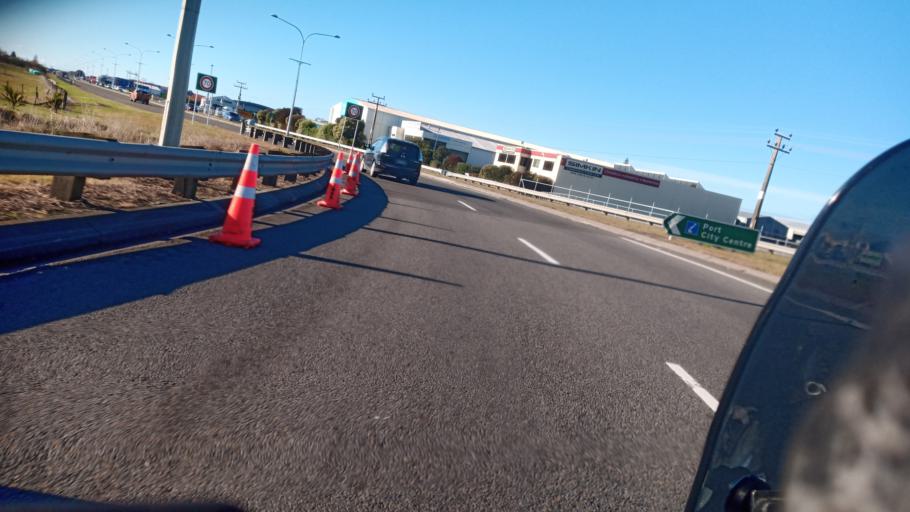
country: NZ
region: Hawke's Bay
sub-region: Napier City
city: Napier
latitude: -39.4961
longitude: 176.8745
